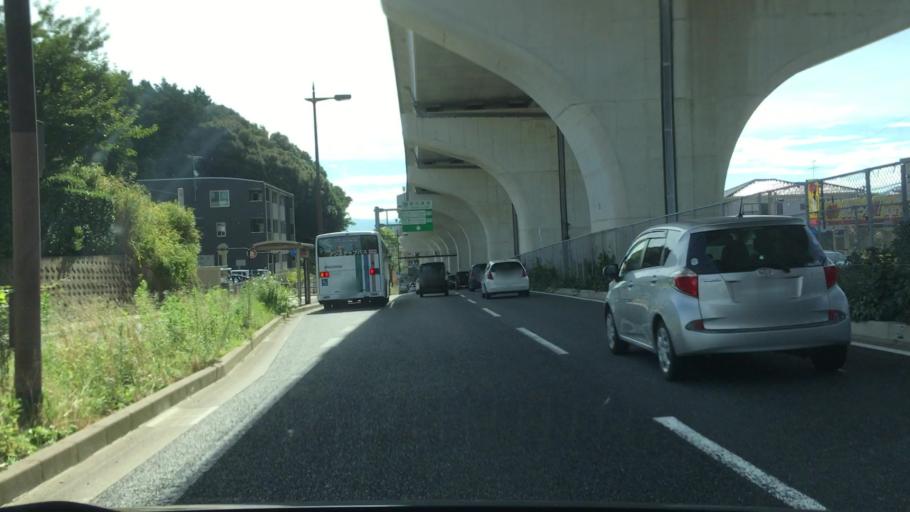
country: JP
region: Fukuoka
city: Maebaru-chuo
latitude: 33.5691
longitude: 130.3033
